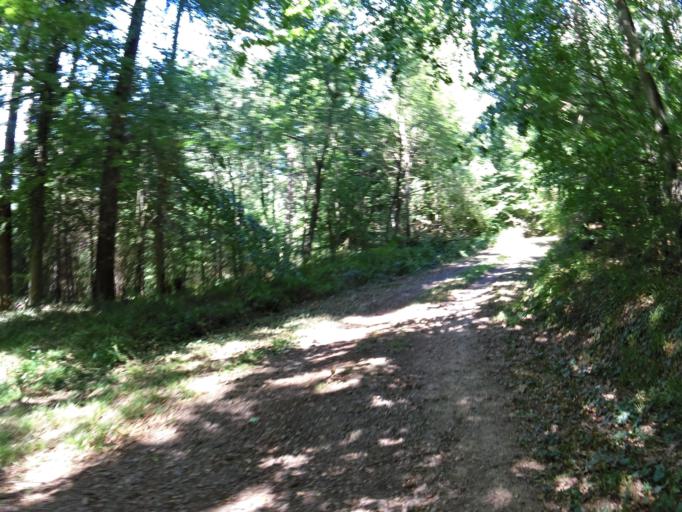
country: DE
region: Baden-Wuerttemberg
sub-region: Freiburg Region
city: Hohberg
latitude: 48.3292
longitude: 7.8994
